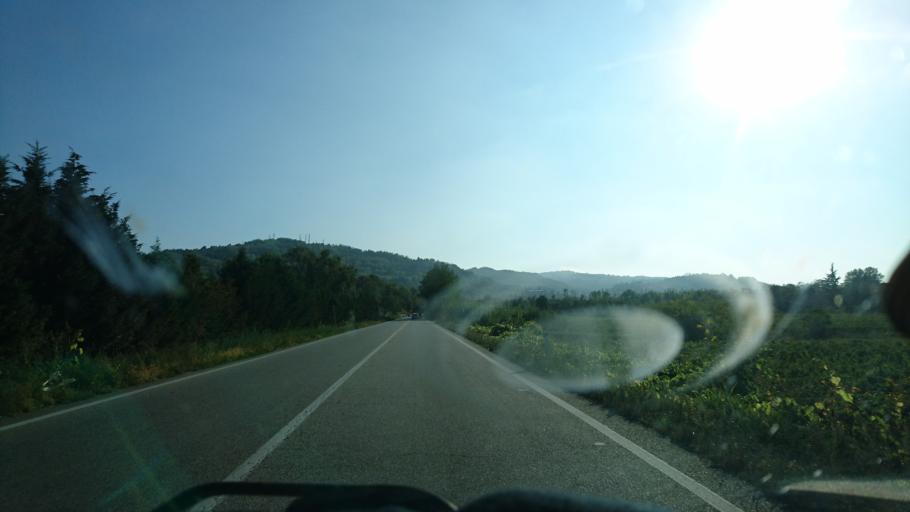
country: IT
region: Piedmont
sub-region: Provincia di Alessandria
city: Visone
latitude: 44.6753
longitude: 8.4859
